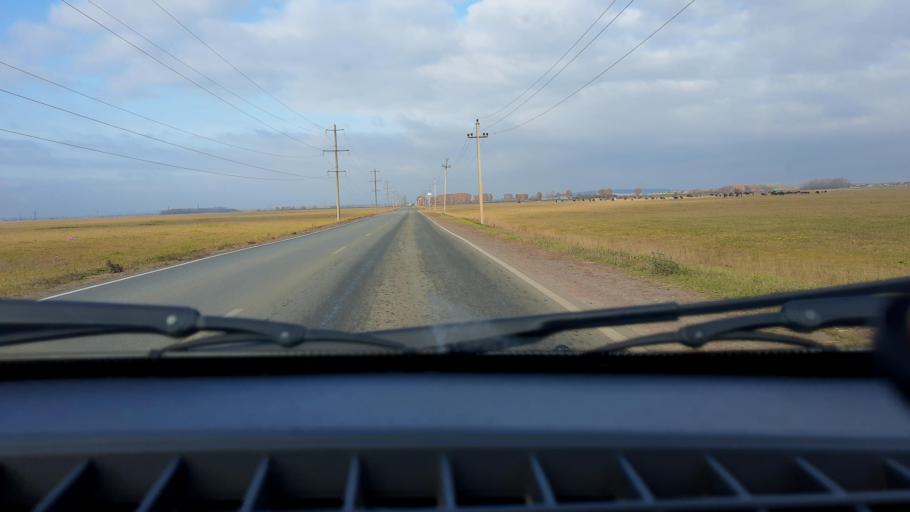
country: RU
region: Bashkortostan
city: Kabakovo
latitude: 54.5376
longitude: 56.0679
